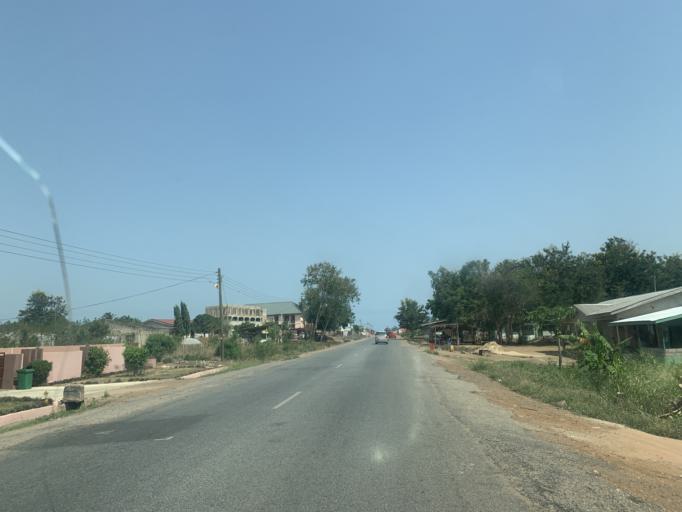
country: GH
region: Central
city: Winneba
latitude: 5.3999
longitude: -0.6505
